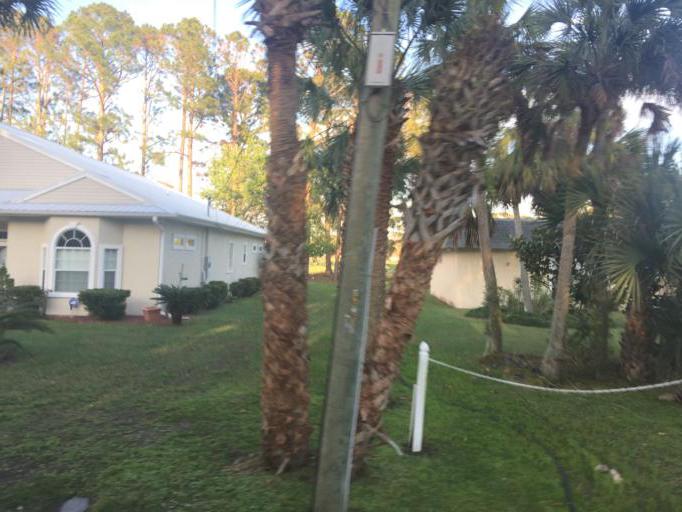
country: US
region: Florida
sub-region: Bay County
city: Panama City Beach
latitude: 30.2176
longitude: -85.8446
